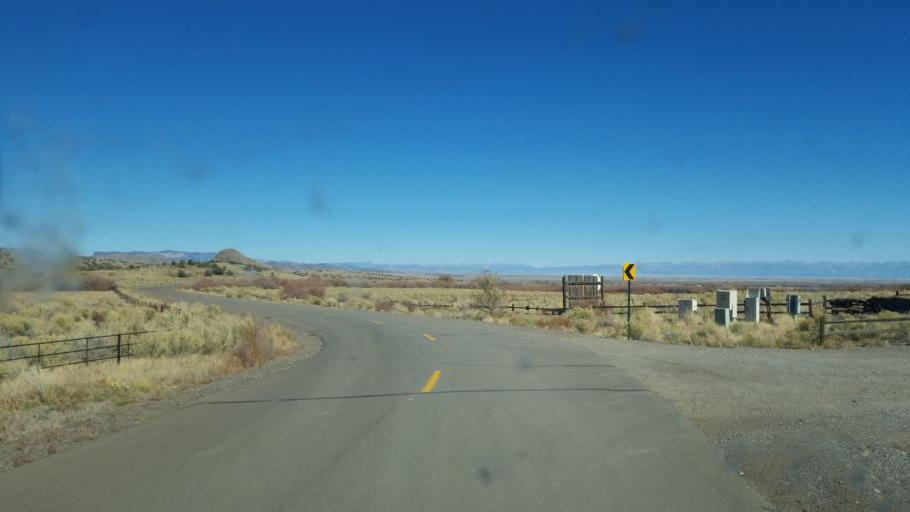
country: US
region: Colorado
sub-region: Rio Grande County
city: Del Norte
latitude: 37.6400
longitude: -106.3649
